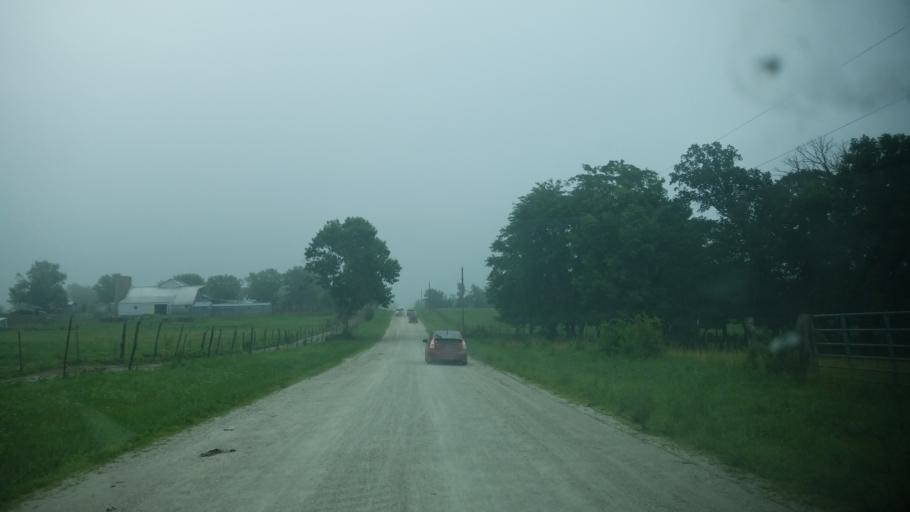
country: US
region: Missouri
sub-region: Pike County
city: Bowling Green
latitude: 39.3087
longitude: -91.3213
